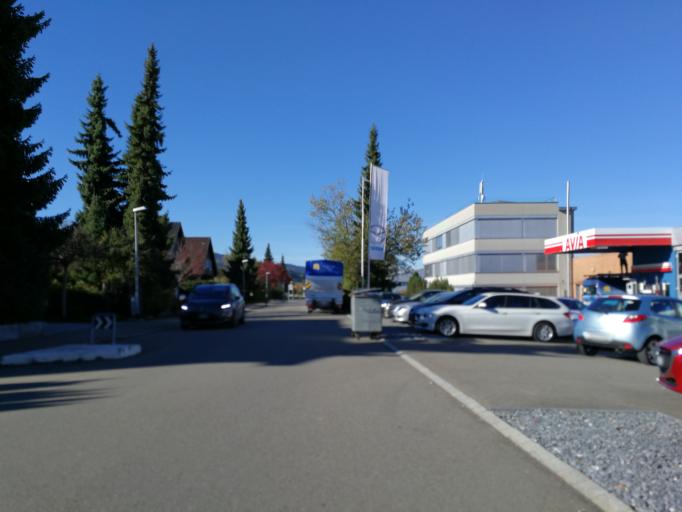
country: CH
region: Zurich
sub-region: Bezirk Meilen
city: Oetwil am See
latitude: 47.2739
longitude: 8.7252
